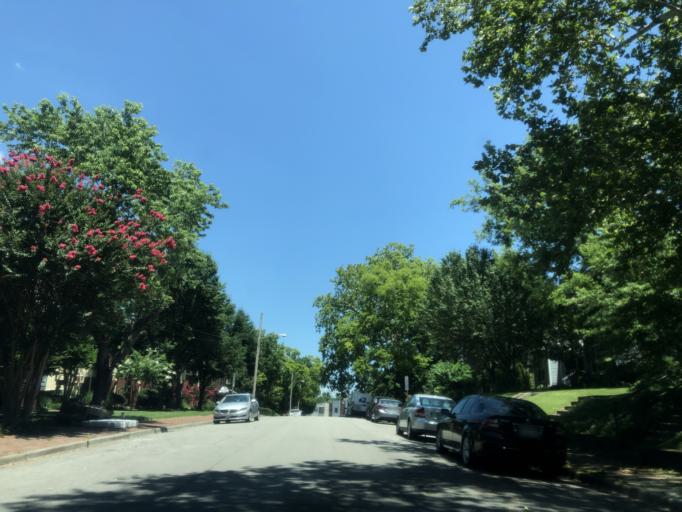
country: US
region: Tennessee
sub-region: Davidson County
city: Nashville
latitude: 36.1747
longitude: -86.7538
